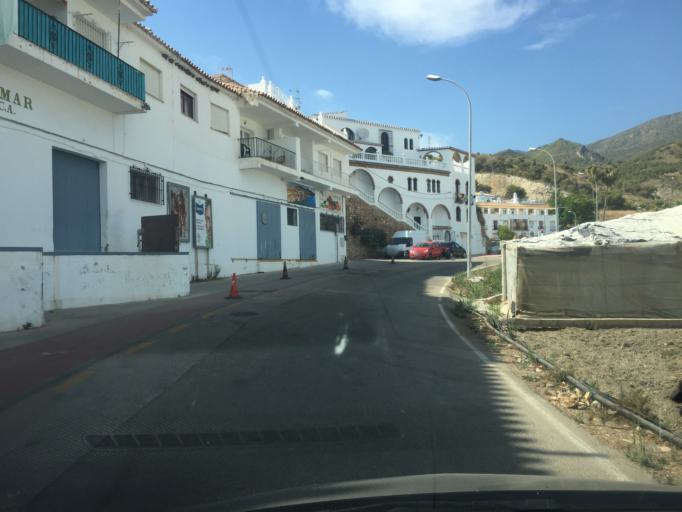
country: ES
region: Andalusia
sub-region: Provincia de Malaga
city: Nerja
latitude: 36.7578
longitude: -3.8421
